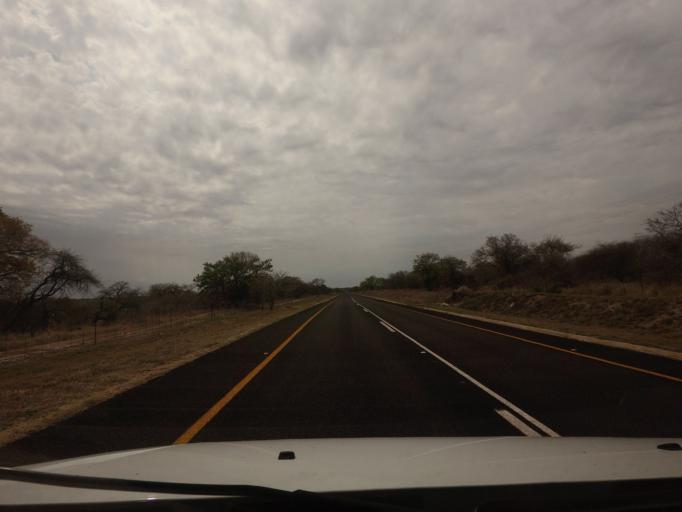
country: ZA
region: Limpopo
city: Thulamahashi
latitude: -24.5535
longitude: 31.1931
